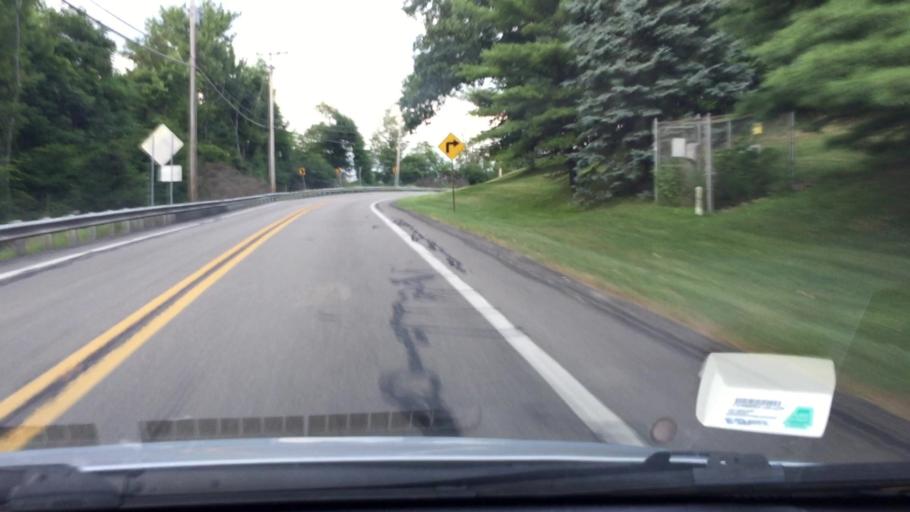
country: US
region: Pennsylvania
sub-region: Allegheny County
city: Gibsonia
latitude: 40.6286
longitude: -80.0172
